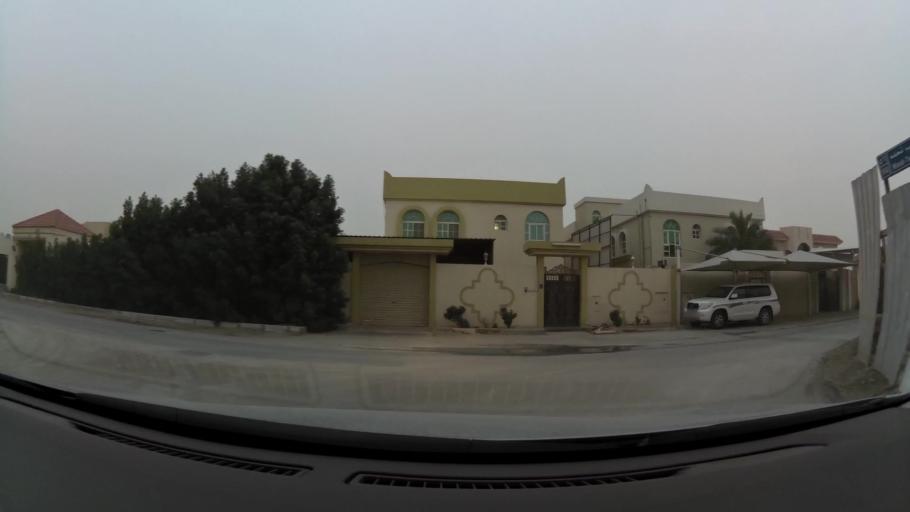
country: QA
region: Baladiyat ad Dawhah
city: Doha
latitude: 25.2334
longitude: 51.4945
